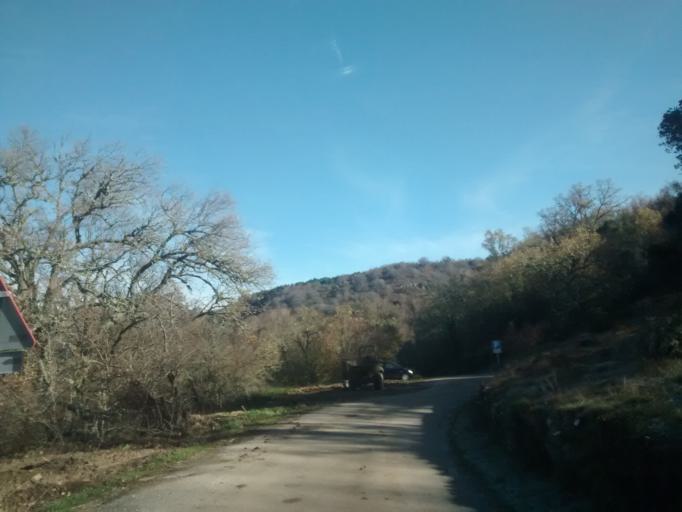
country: ES
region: Cantabria
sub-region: Provincia de Cantabria
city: San Pedro del Romeral
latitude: 42.9686
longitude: -3.7473
